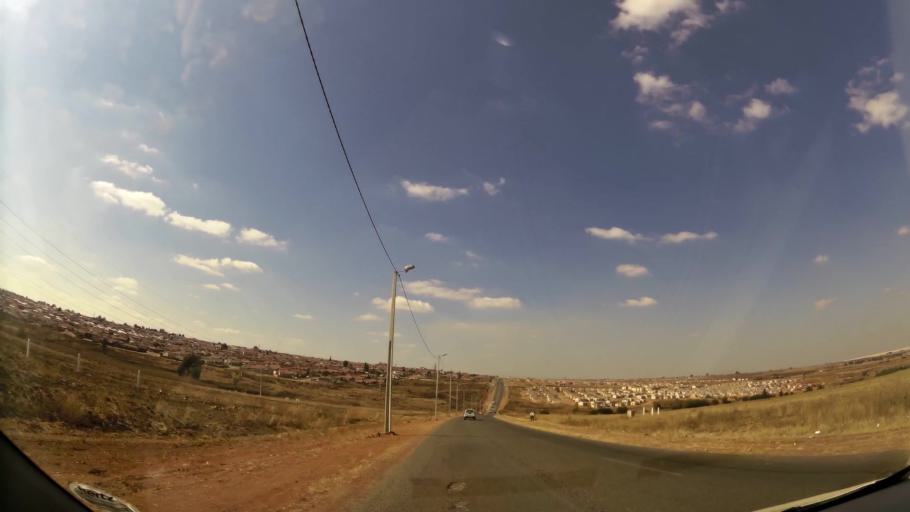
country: ZA
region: Gauteng
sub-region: West Rand District Municipality
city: Randfontein
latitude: -26.1640
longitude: 27.7639
